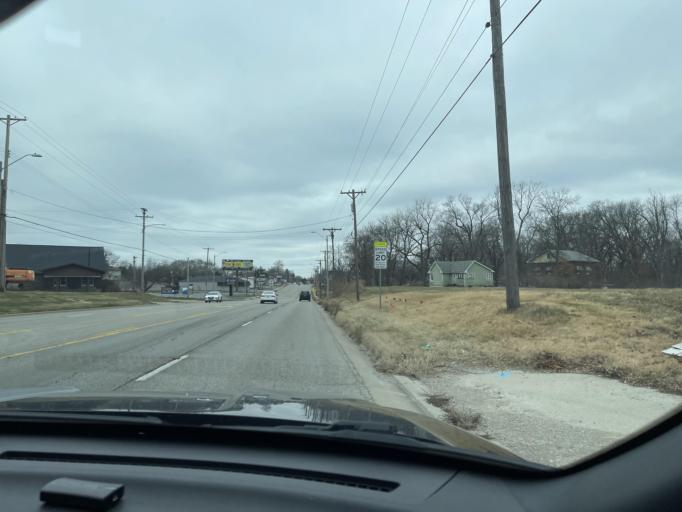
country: US
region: Illinois
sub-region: Sangamon County
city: Leland Grove
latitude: 39.8080
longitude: -89.6816
